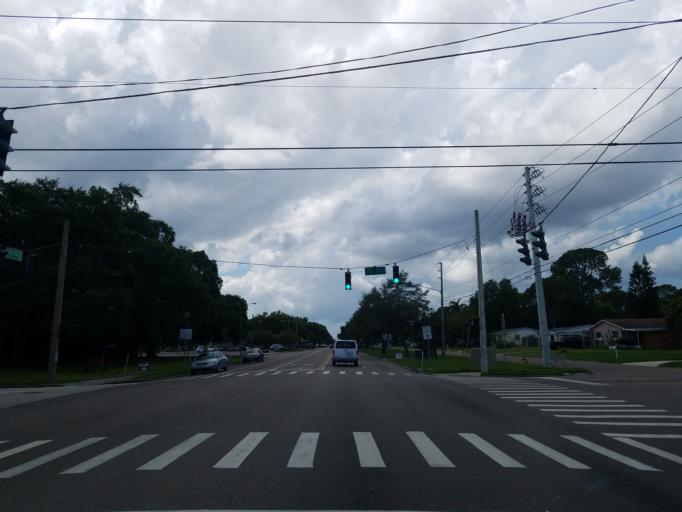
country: US
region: Florida
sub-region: Pinellas County
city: Lealman
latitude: 27.8358
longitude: -82.6469
